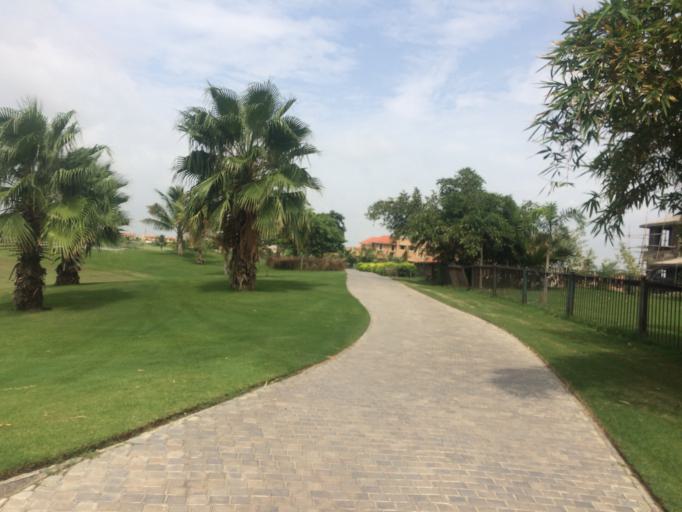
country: IN
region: Gujarat
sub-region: Ahmadabad
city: Sanand
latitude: 23.0227
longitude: 72.3594
